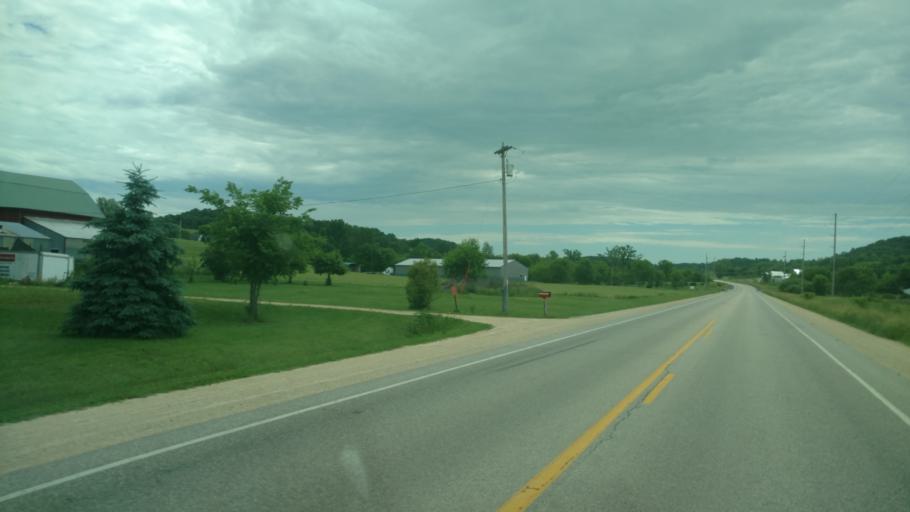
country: US
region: Wisconsin
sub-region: Monroe County
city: Tomah
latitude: 43.8309
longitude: -90.4668
